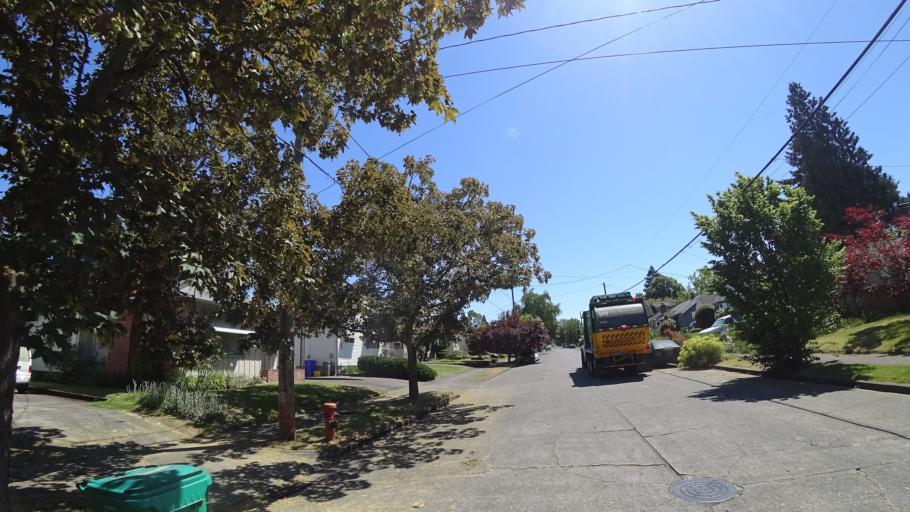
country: US
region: Oregon
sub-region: Multnomah County
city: Portland
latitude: 45.5655
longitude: -122.6521
